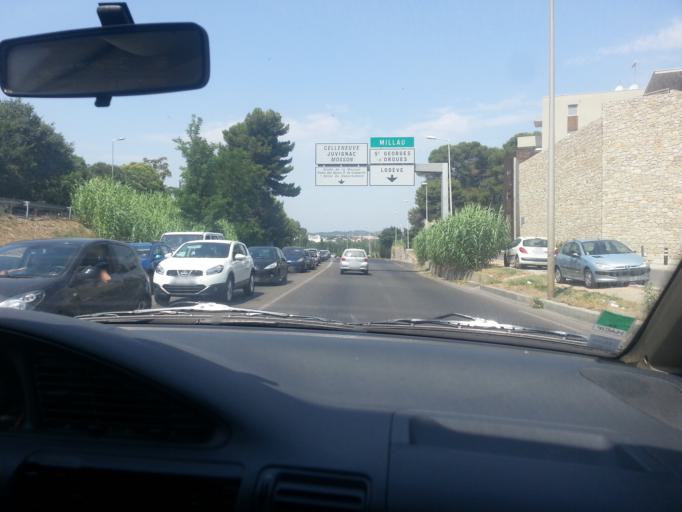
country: FR
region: Languedoc-Roussillon
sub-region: Departement de l'Herault
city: Juvignac
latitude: 43.6116
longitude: 3.8273
